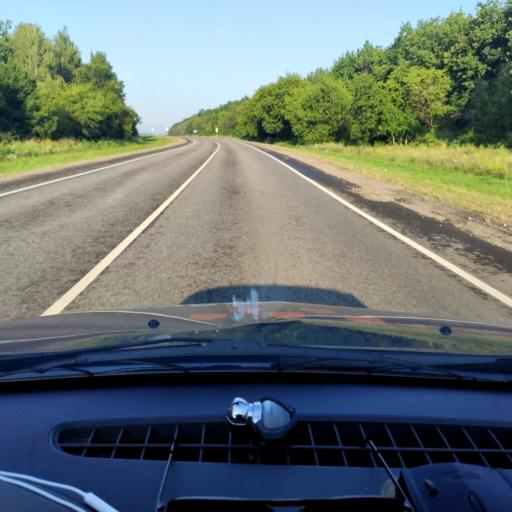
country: RU
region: Lipetsk
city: Izmalkovo
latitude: 52.4474
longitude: 37.9791
